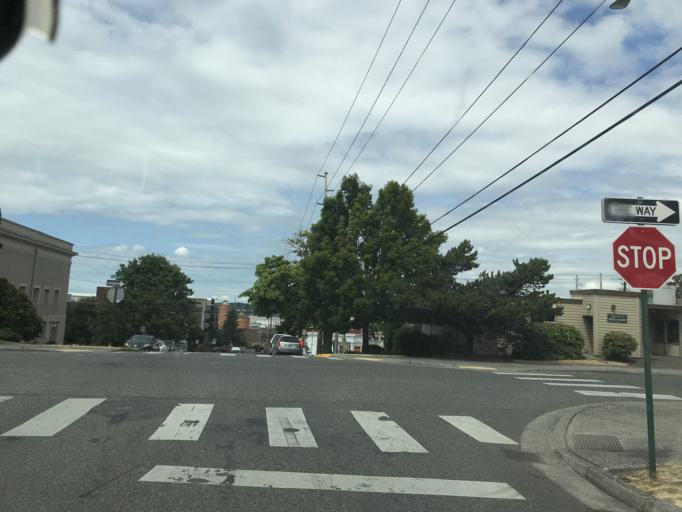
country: US
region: Washington
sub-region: Whatcom County
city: Bellingham
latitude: 48.7456
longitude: -122.4789
